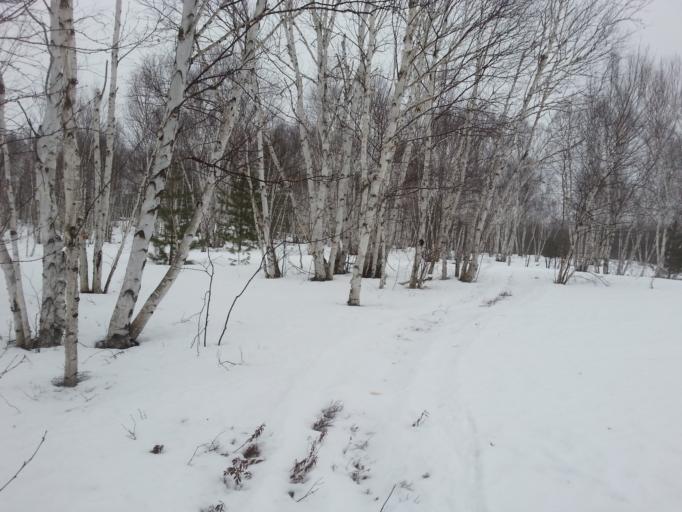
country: CA
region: Ontario
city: Greater Sudbury
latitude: 46.4048
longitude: -80.9884
